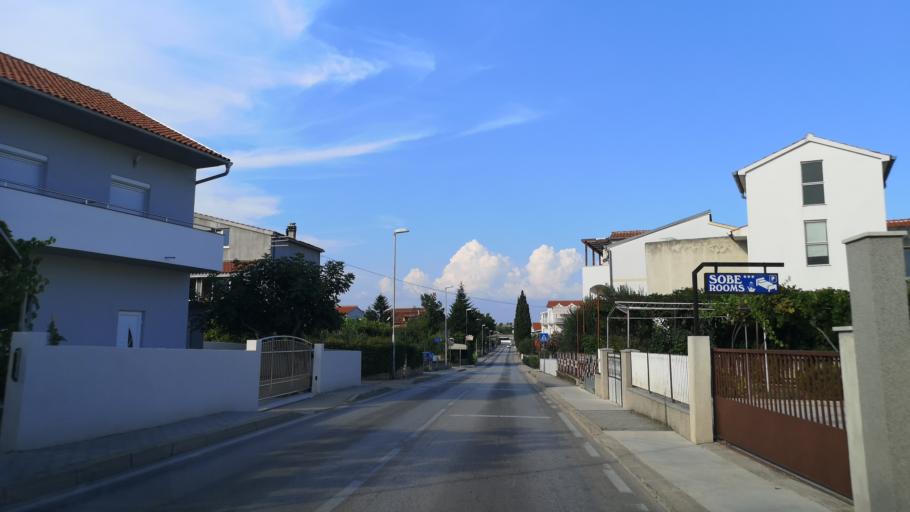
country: HR
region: Sibensko-Kniniska
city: Vodice
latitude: 43.7619
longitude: 15.7717
